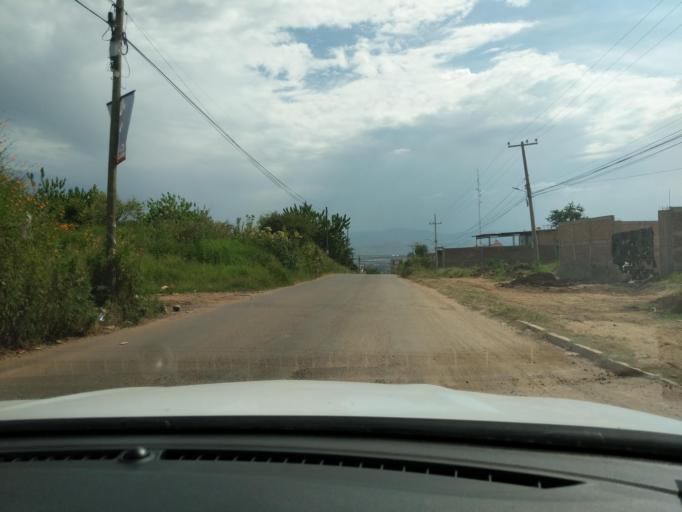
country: MX
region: Jalisco
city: San Jose del Castillo
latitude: 20.5242
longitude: -103.2333
